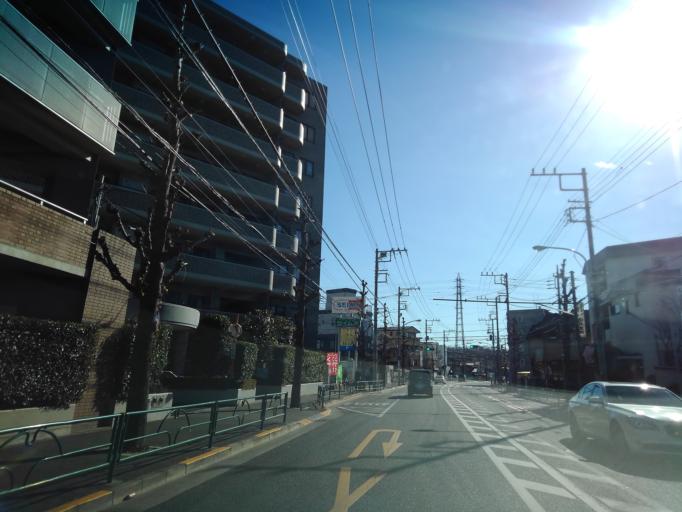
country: JP
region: Tokyo
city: Kokubunji
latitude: 35.6864
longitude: 139.4992
